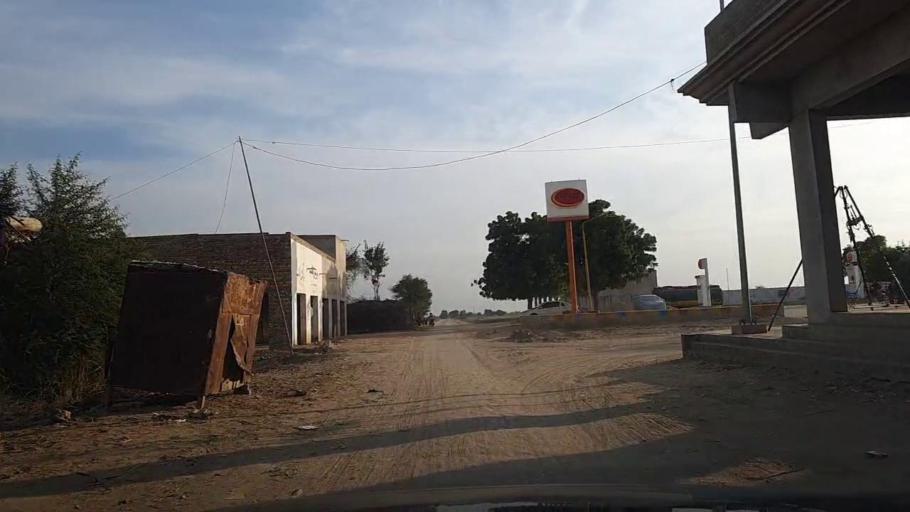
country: PK
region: Sindh
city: Jam Sahib
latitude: 26.4468
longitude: 68.5718
